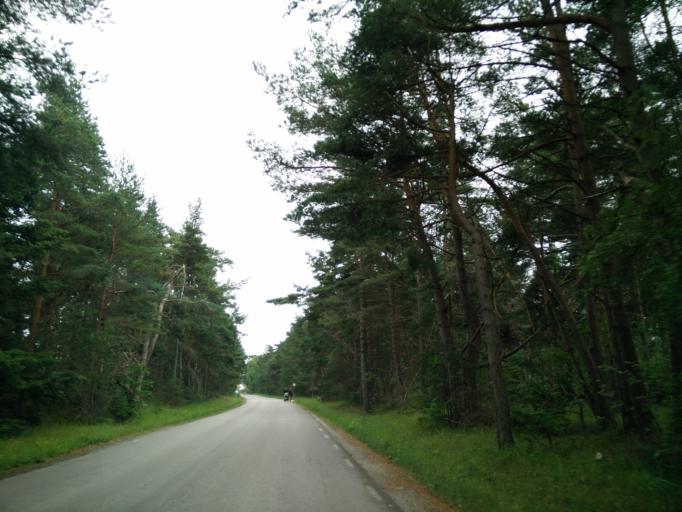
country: SE
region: Gotland
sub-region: Gotland
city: Slite
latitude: 57.9647
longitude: 19.2370
